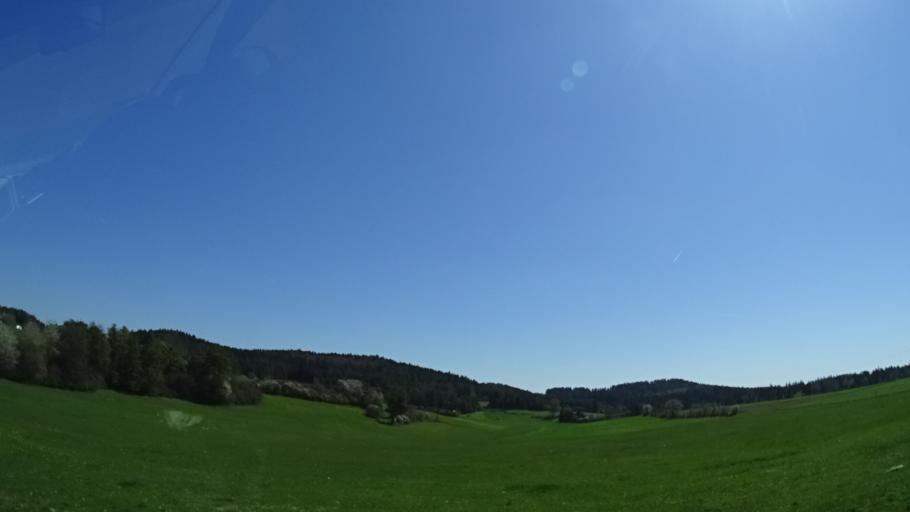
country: DE
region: Bavaria
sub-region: Upper Palatinate
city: Kastl
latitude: 49.3848
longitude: 11.7037
